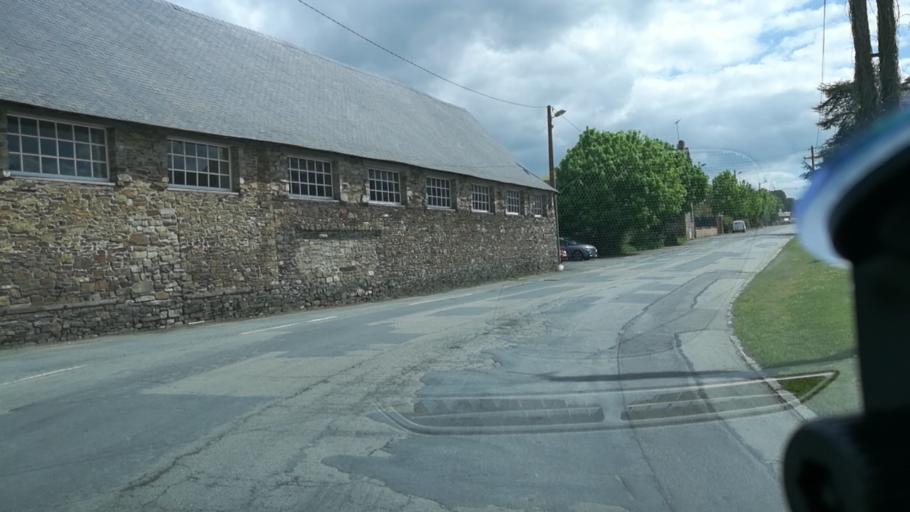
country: FR
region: Brittany
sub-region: Departement d'Ille-et-Vilaine
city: Martigne-Ferchaud
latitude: 47.8363
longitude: -1.3226
